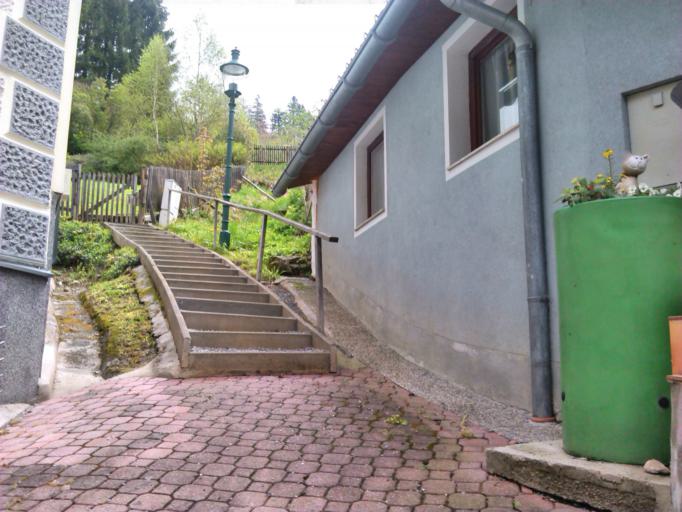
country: AT
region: Styria
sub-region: Politischer Bezirk Bruck-Muerzzuschlag
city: Mariazell
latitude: 47.7737
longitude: 15.3224
